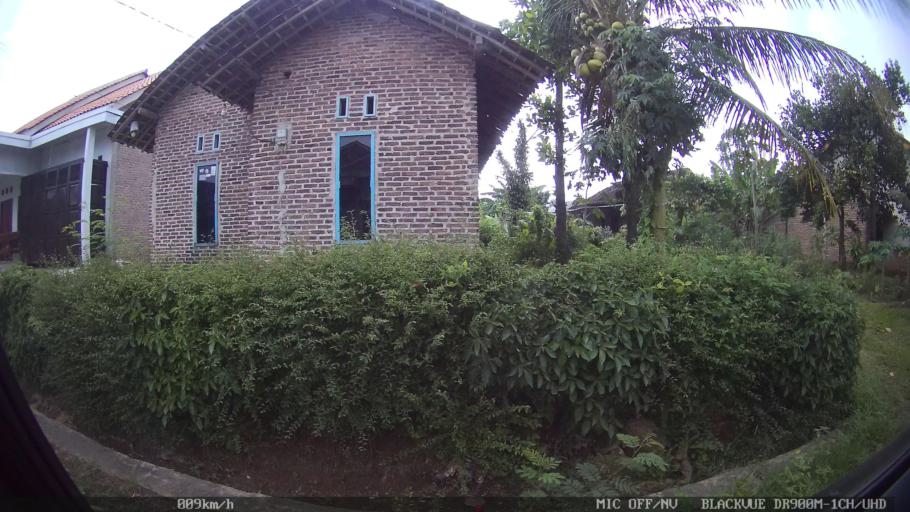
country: ID
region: Lampung
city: Gadingrejo
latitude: -5.3675
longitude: 105.0659
